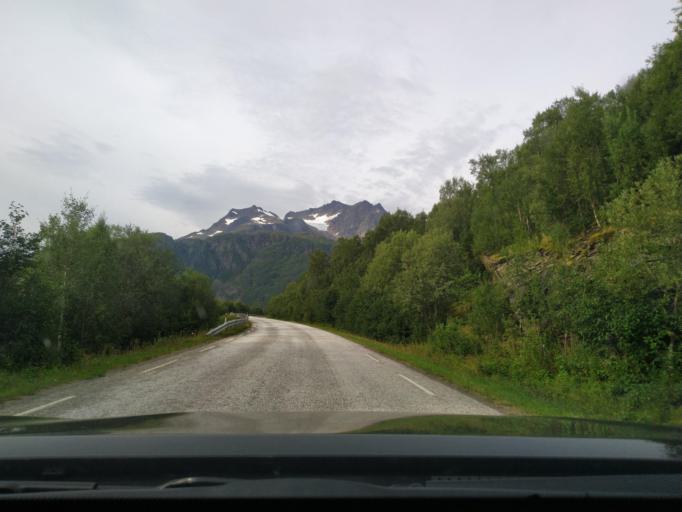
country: NO
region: Troms
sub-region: Dyroy
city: Brostadbotn
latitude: 68.9014
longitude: 17.4804
